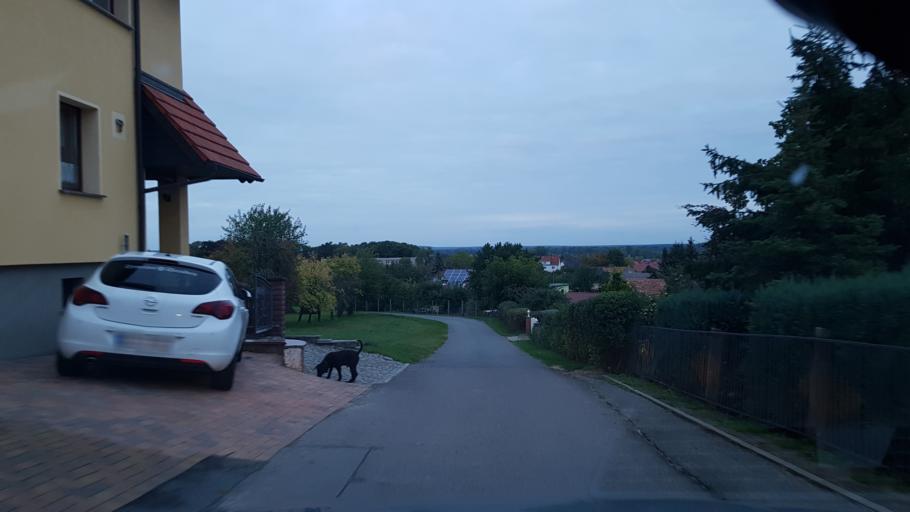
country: DE
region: Brandenburg
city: Hirschfeld
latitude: 51.3841
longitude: 13.6127
